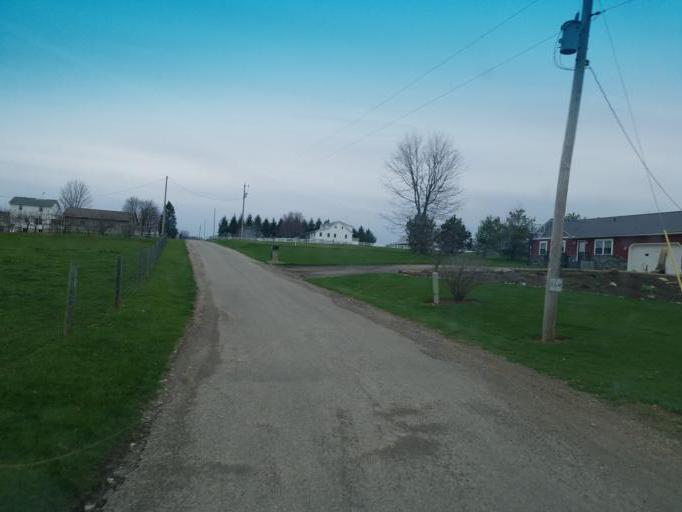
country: US
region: Ohio
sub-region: Holmes County
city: Millersburg
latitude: 40.6525
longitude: -81.9144
